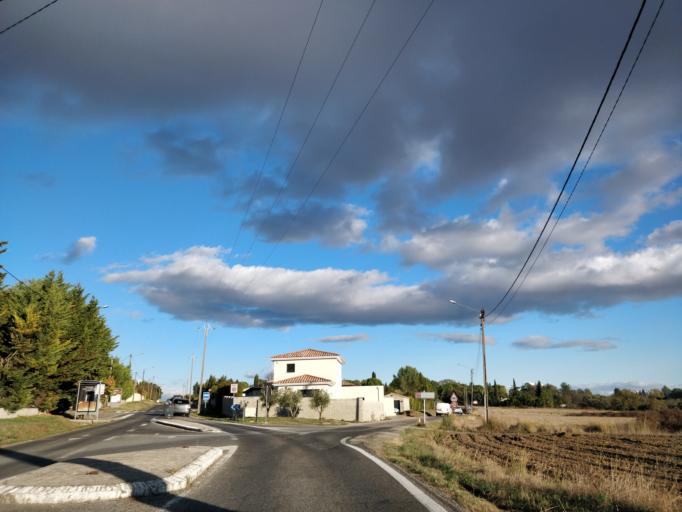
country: FR
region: Languedoc-Roussillon
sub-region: Departement de l'Herault
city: Saint-Drezery
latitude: 43.7278
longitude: 3.9636
